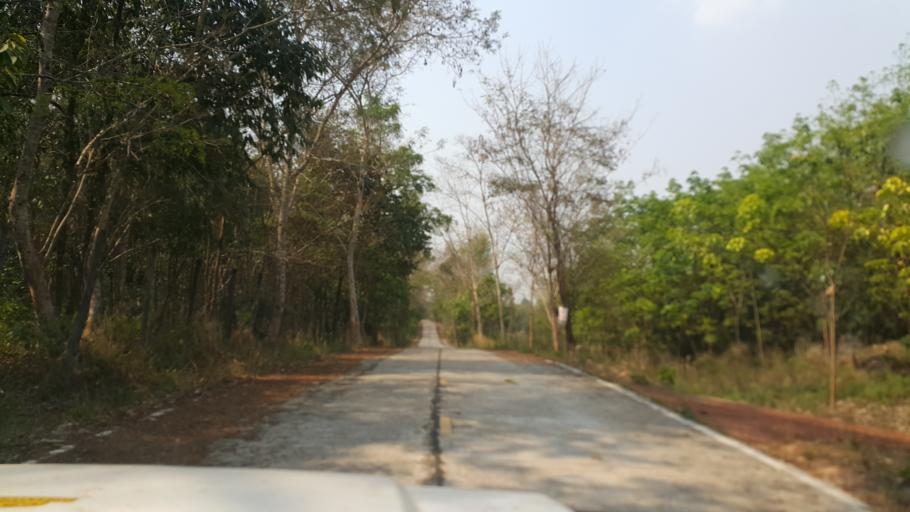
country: TH
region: Nakhon Phanom
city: Ban Phaeng
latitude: 17.9795
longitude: 104.1481
